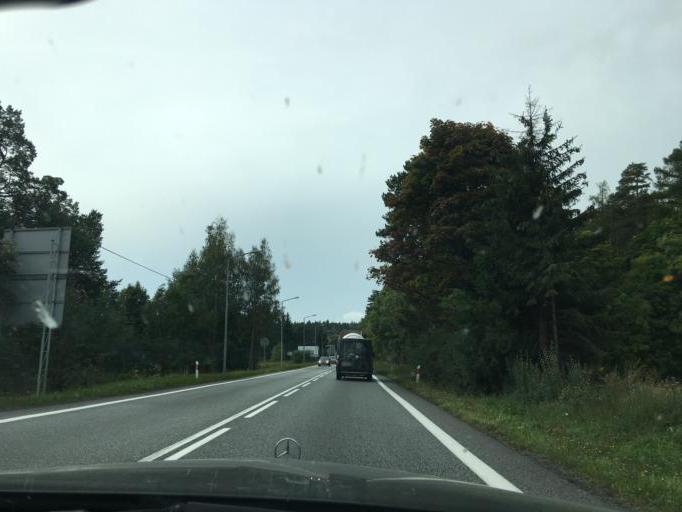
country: PL
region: Lower Silesian Voivodeship
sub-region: Powiat klodzki
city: Polanica-Zdroj
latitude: 50.4228
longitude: 16.5054
